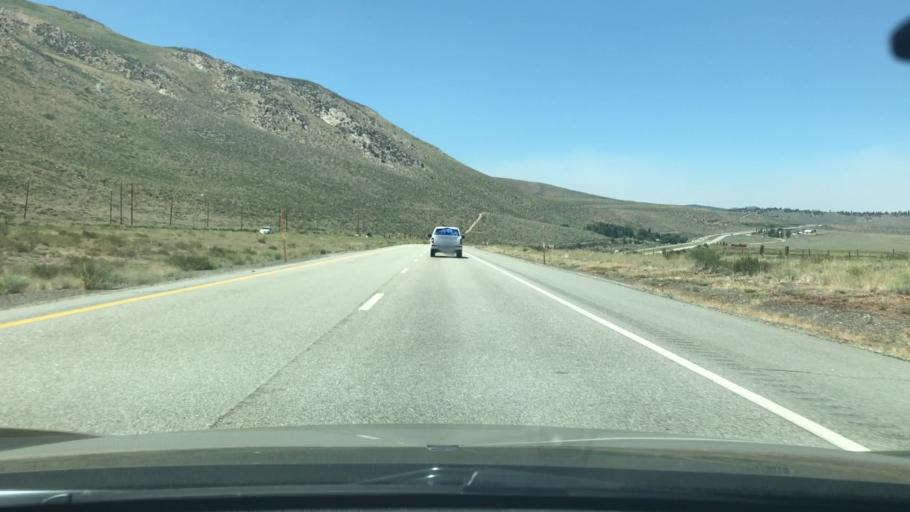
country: US
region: California
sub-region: Mono County
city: Mammoth Lakes
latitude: 37.5895
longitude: -118.7878
